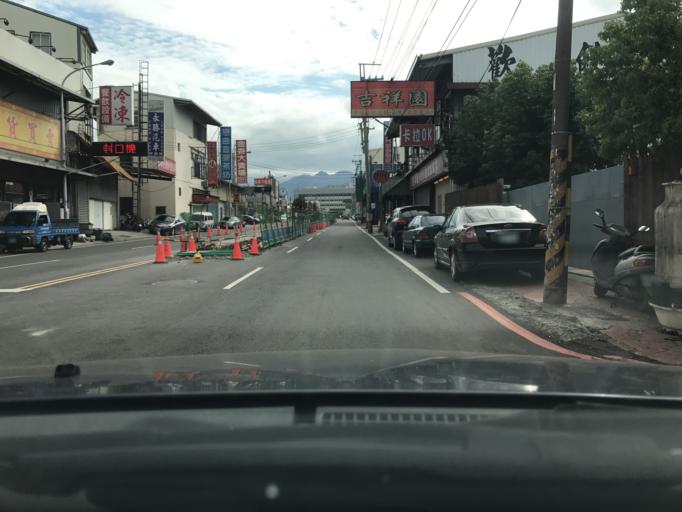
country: TW
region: Taiwan
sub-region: Hsinchu
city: Zhubei
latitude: 24.7266
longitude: 121.0994
